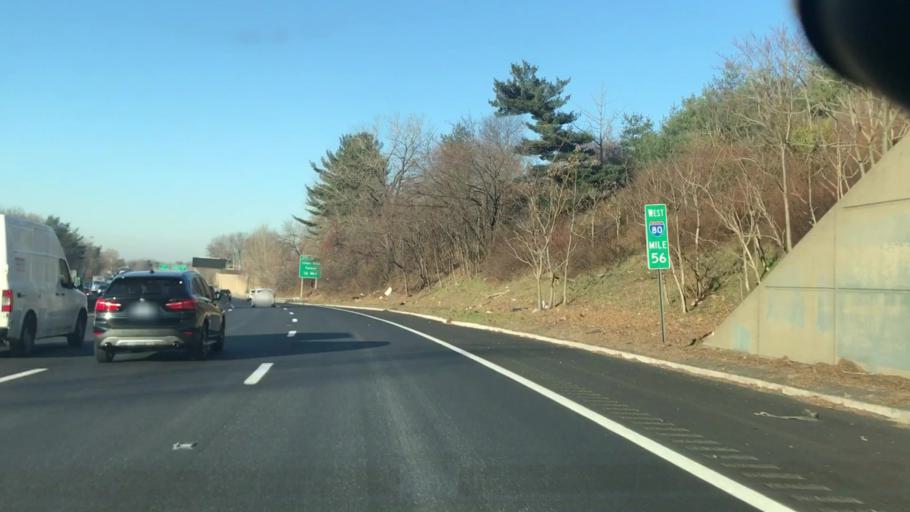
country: US
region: New Jersey
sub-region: Passaic County
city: Totowa
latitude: 40.8976
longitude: -74.2105
